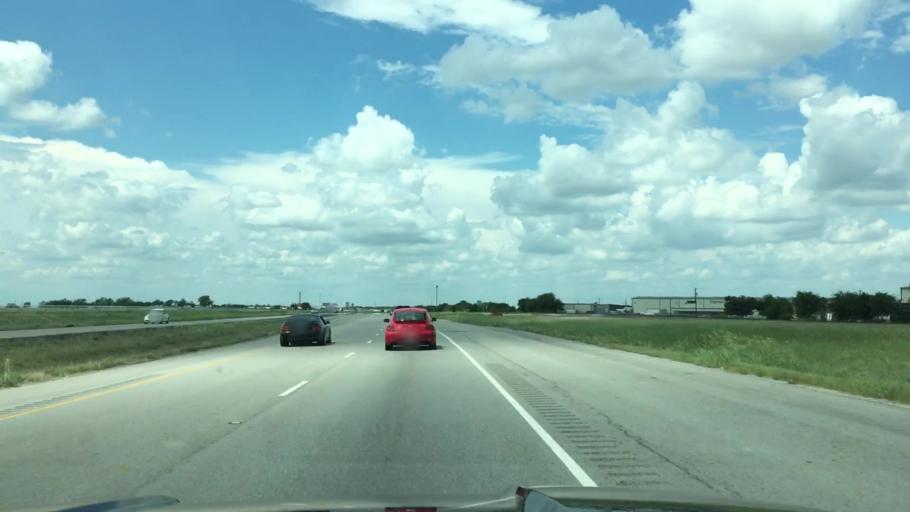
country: US
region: Texas
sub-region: Wise County
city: Rhome
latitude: 33.0238
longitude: -97.4435
